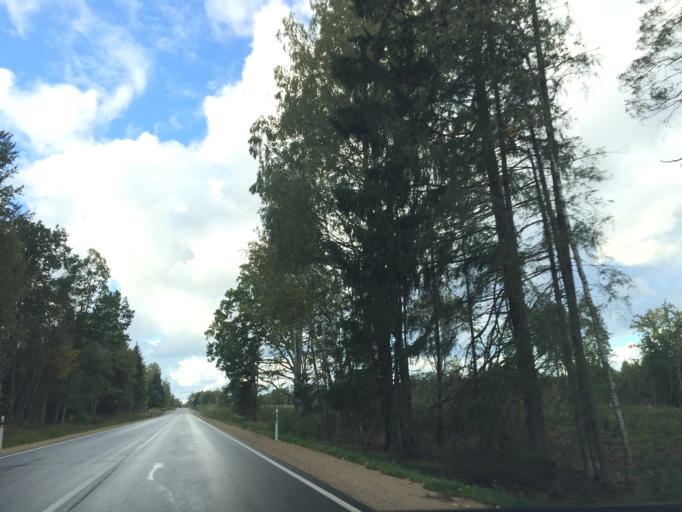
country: LV
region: Ligatne
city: Ligatne
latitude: 57.1675
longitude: 25.0470
